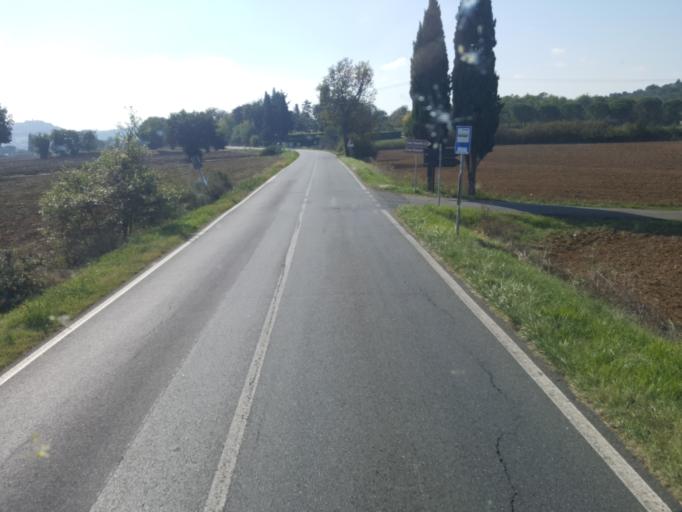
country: IT
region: Tuscany
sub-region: Provincia di Siena
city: Casole d'Elsa
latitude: 43.3746
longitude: 11.0686
